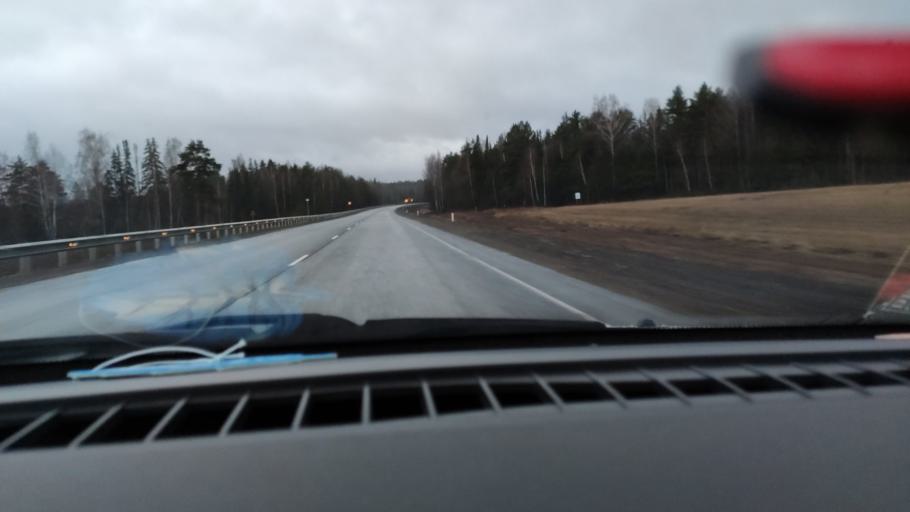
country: RU
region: Udmurtiya
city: Alnashi
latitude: 56.1075
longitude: 52.4602
